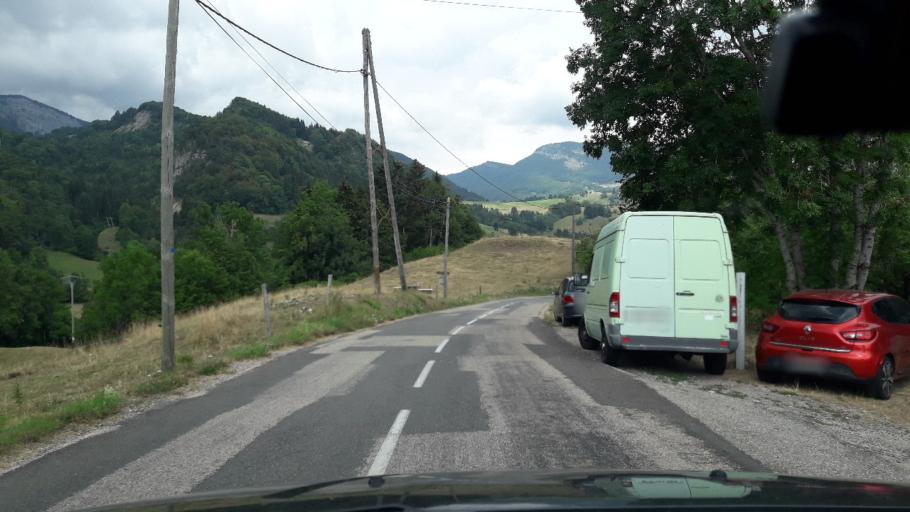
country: FR
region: Rhone-Alpes
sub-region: Departement de la Savoie
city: Vimines
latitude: 45.4478
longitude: 5.8739
